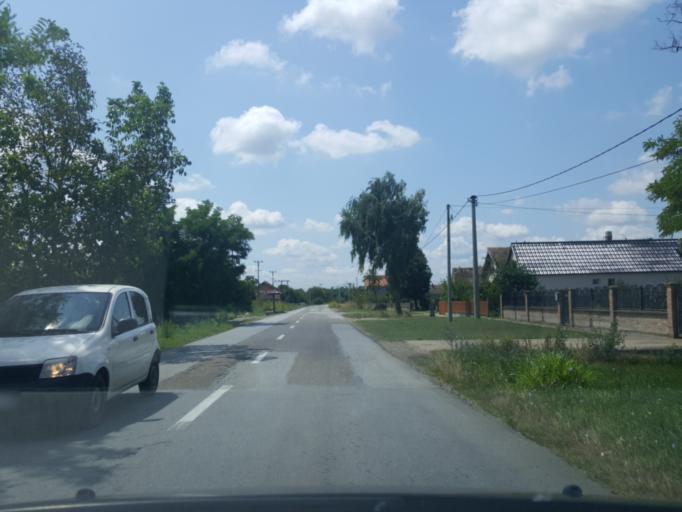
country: RS
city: Salas Nocajski
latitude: 44.9339
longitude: 19.5694
